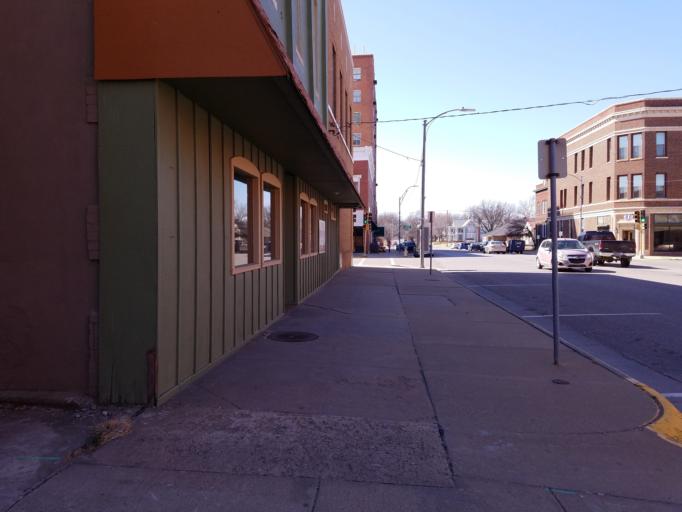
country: US
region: Kansas
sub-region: Dickinson County
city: Abilene
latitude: 38.9172
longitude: -97.2161
